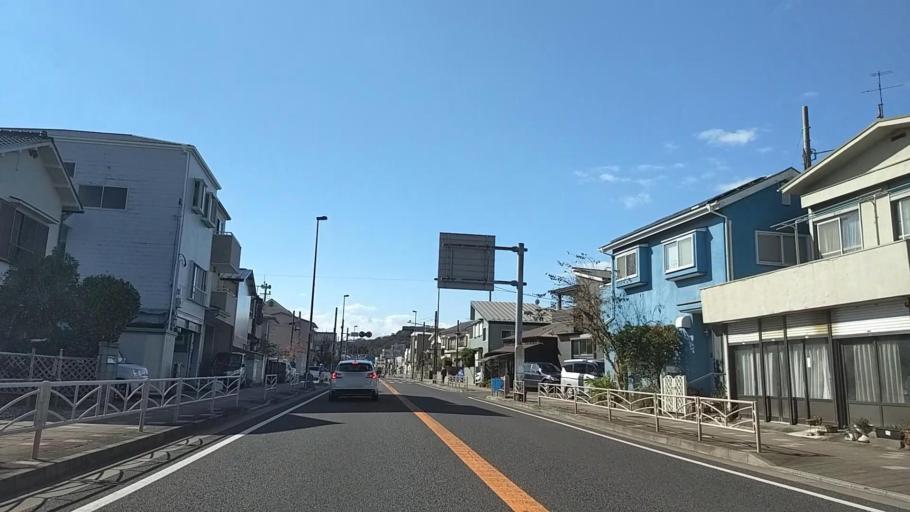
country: JP
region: Kanagawa
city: Oiso
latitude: 35.3137
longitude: 139.3198
